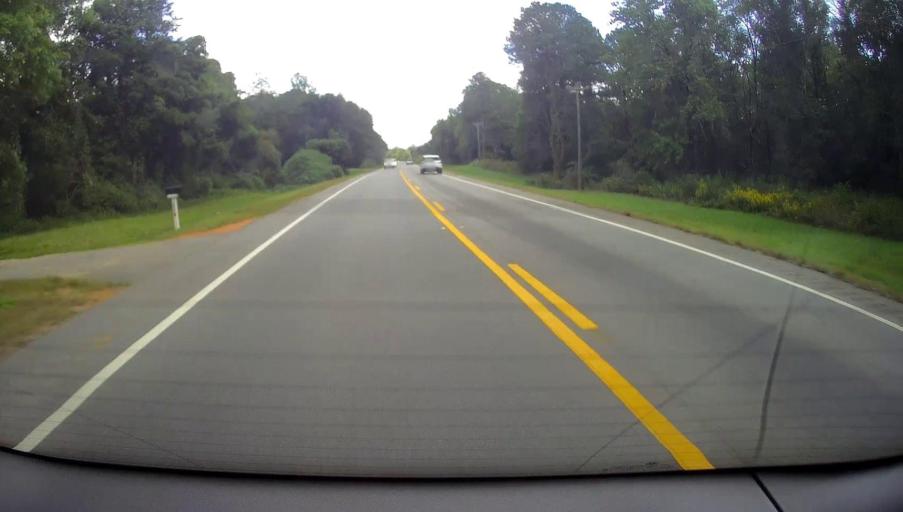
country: US
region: Georgia
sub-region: Baldwin County
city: Milledgeville
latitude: 33.0747
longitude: -83.3300
